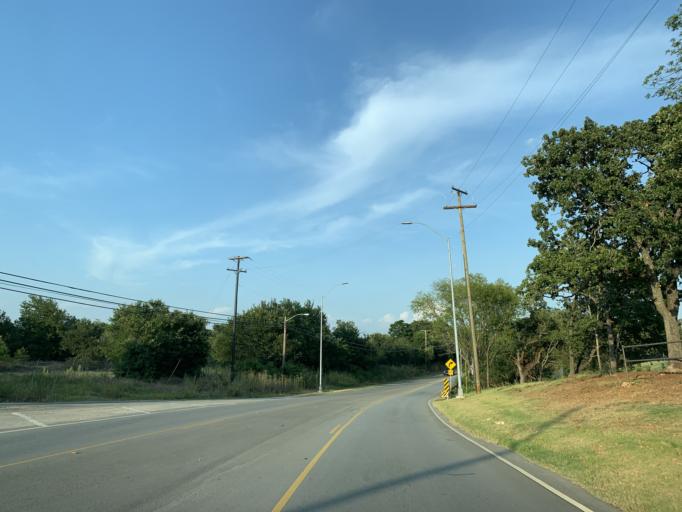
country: US
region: Texas
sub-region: Tarrant County
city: Richland Hills
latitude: 32.7797
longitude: -97.2081
